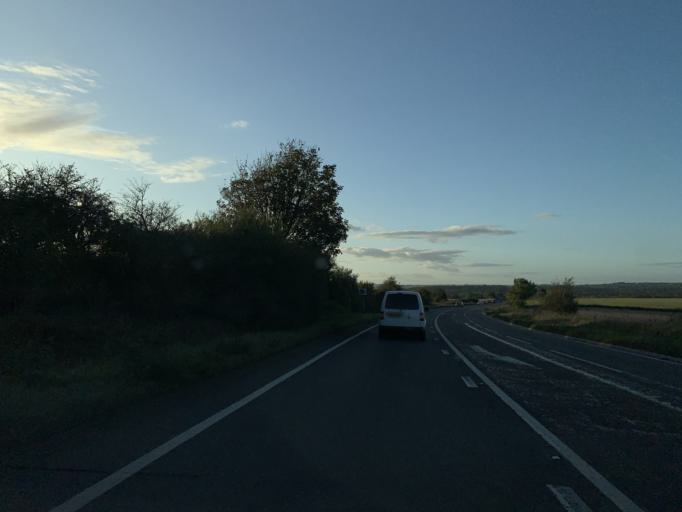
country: GB
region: England
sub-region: Wiltshire
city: Alderbury
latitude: 51.0237
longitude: -1.7073
